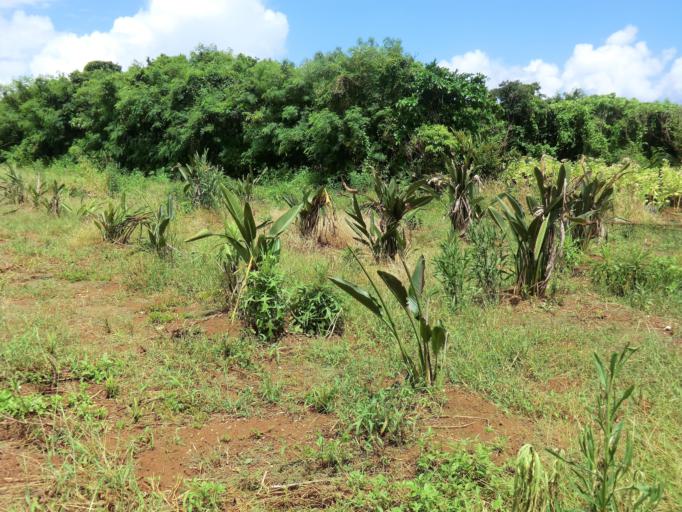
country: JP
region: Okinawa
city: Itoman
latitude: 26.0836
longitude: 127.6759
